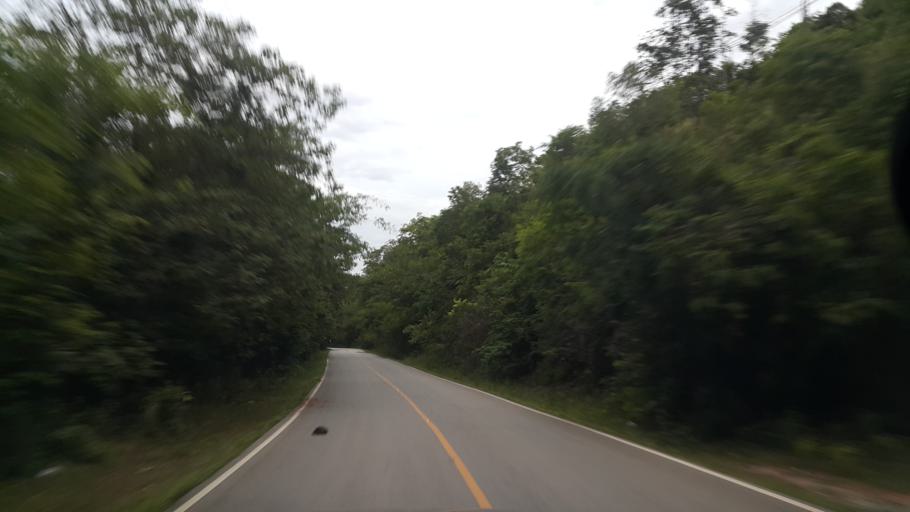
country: TH
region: Loei
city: Na Haeo
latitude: 17.5299
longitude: 101.2016
